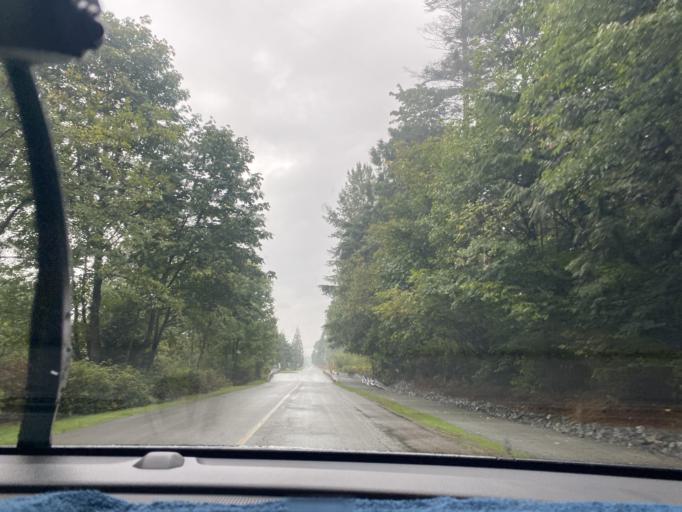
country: CA
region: British Columbia
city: Agassiz
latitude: 49.2846
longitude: -121.7775
